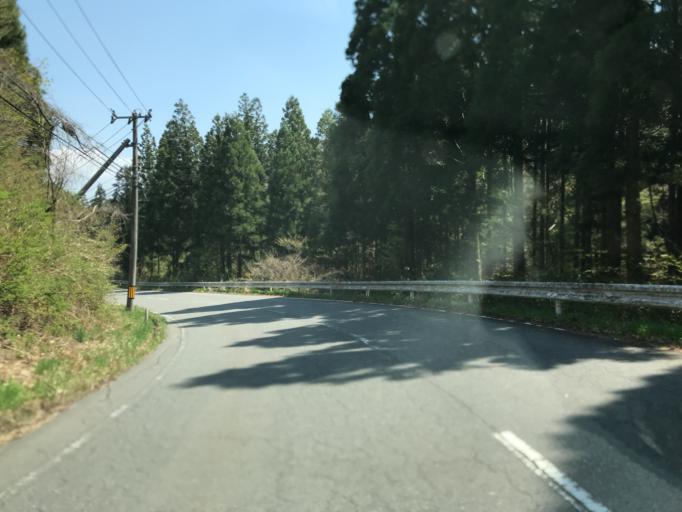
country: JP
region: Ibaraki
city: Kitaibaraki
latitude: 36.9760
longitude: 140.6313
